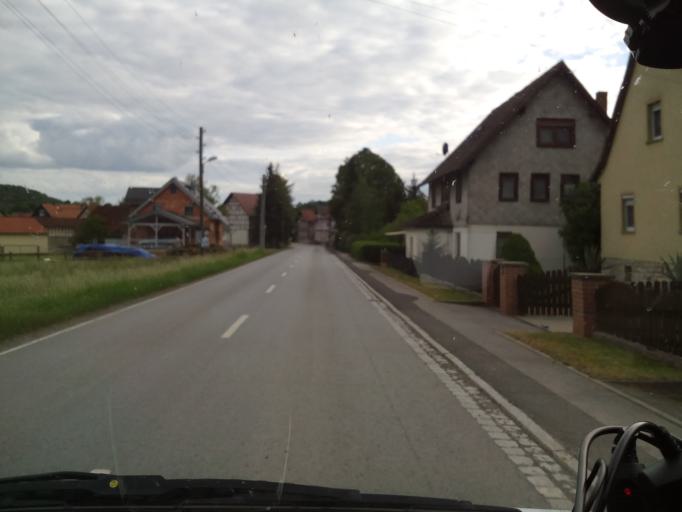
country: DE
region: Thuringia
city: Hellingen
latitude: 50.2557
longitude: 10.6840
